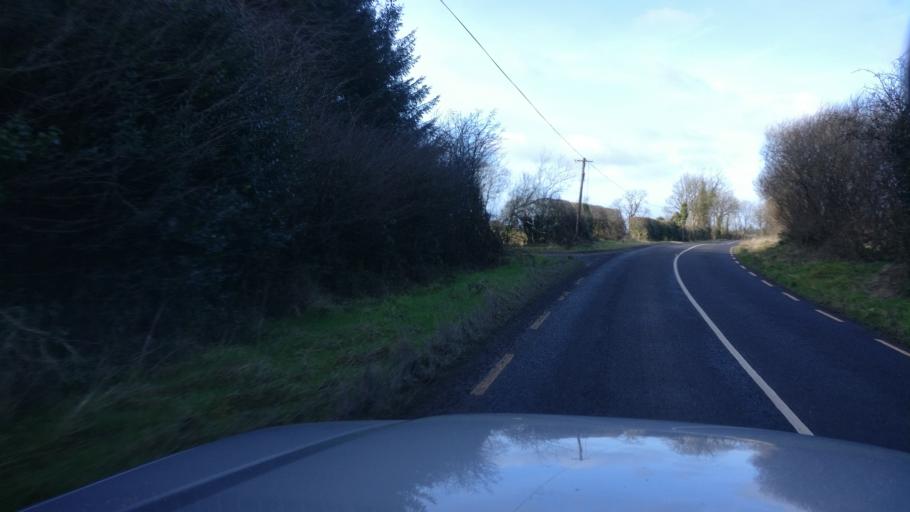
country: IE
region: Leinster
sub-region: Laois
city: Stradbally
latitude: 52.9159
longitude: -7.1863
